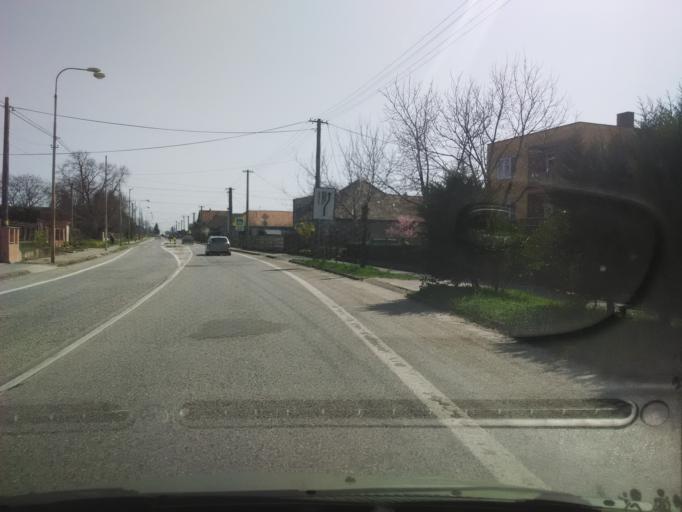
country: SK
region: Nitriansky
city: Surany
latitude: 48.0906
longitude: 18.0669
